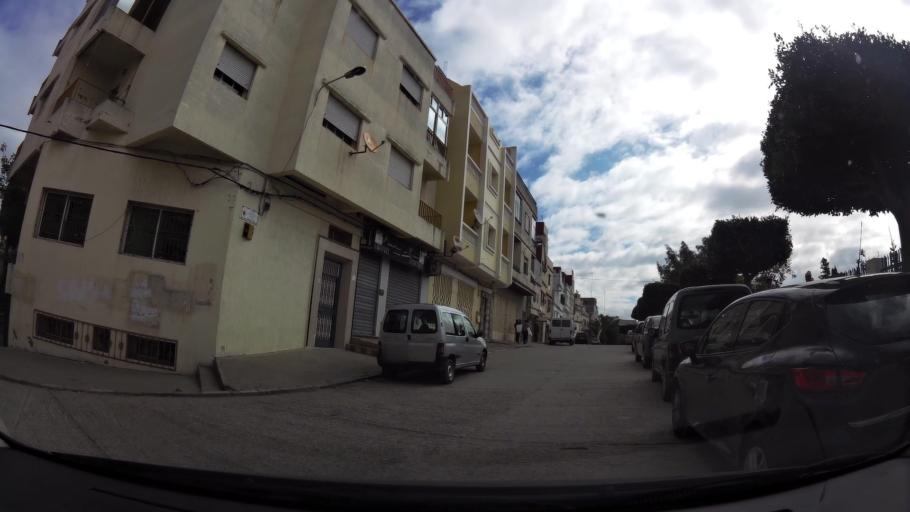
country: MA
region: Tanger-Tetouan
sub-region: Tanger-Assilah
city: Tangier
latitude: 35.7743
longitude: -5.8196
